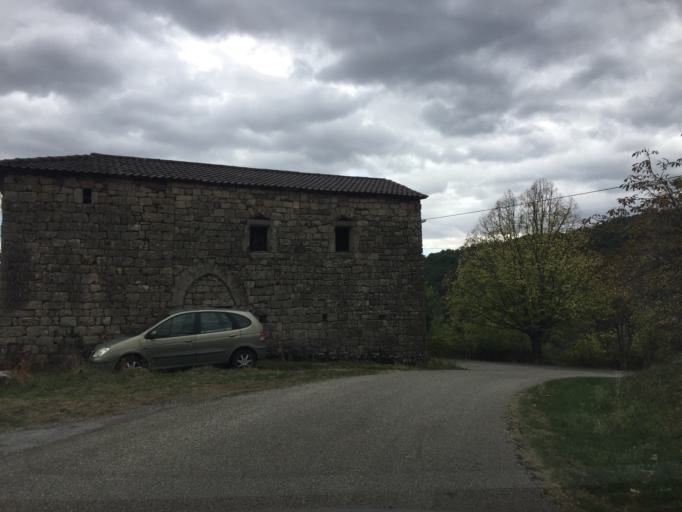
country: FR
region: Rhone-Alpes
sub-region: Departement de l'Ardeche
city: Les Vans
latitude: 44.4262
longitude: 4.0821
